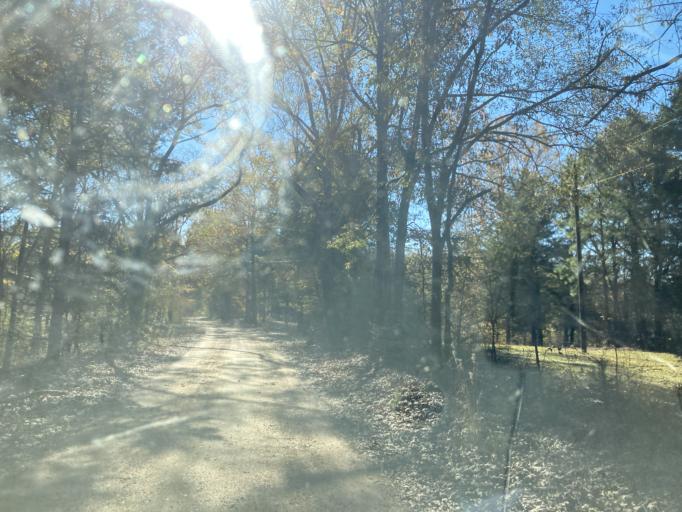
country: US
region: Mississippi
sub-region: Hinds County
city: Lynchburg
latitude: 32.5947
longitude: -90.4950
